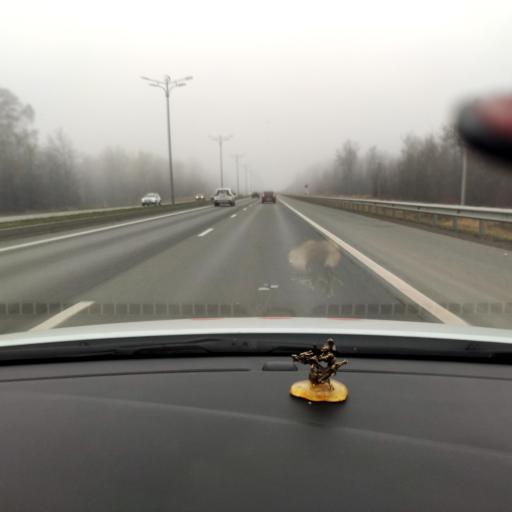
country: RU
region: Tatarstan
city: Stolbishchi
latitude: 55.7038
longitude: 49.2233
